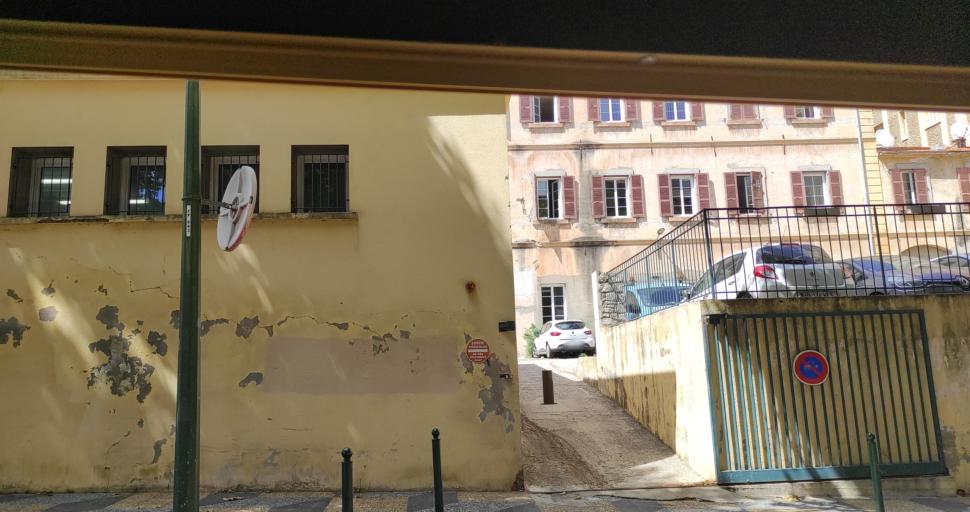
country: FR
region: Corsica
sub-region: Departement de la Corse-du-Sud
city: Ajaccio
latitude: 41.9174
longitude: 8.7291
